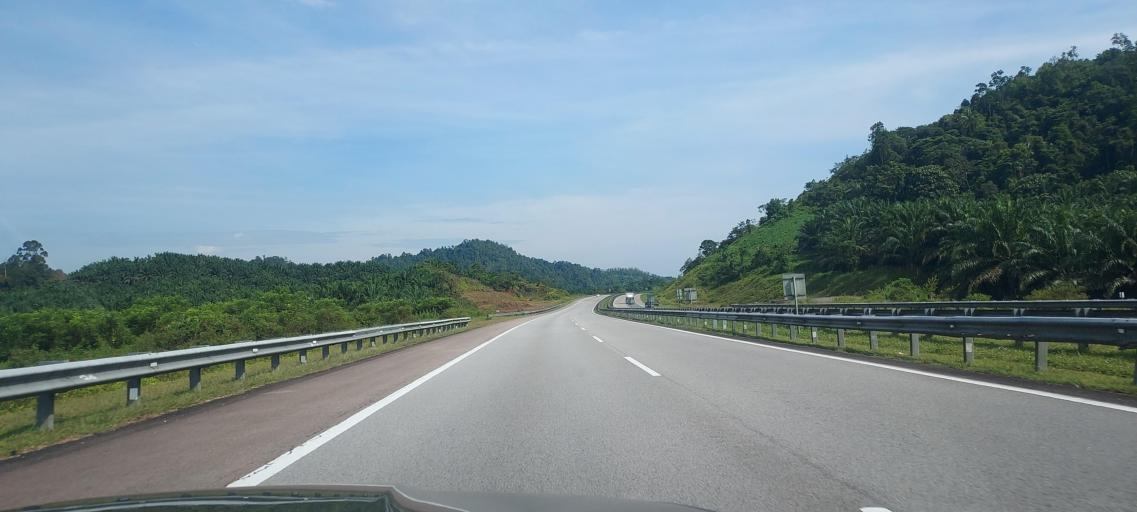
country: MY
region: Terengganu
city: Marang
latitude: 4.9450
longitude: 103.0930
